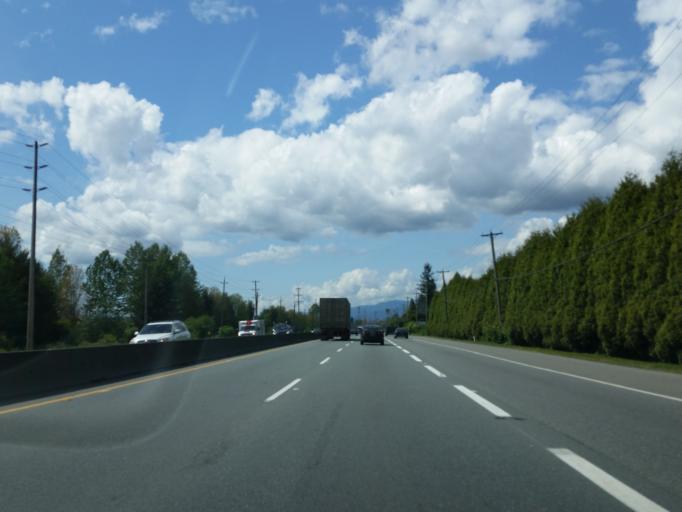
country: CA
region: British Columbia
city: Pitt Meadows
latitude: 49.2390
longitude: -122.7096
